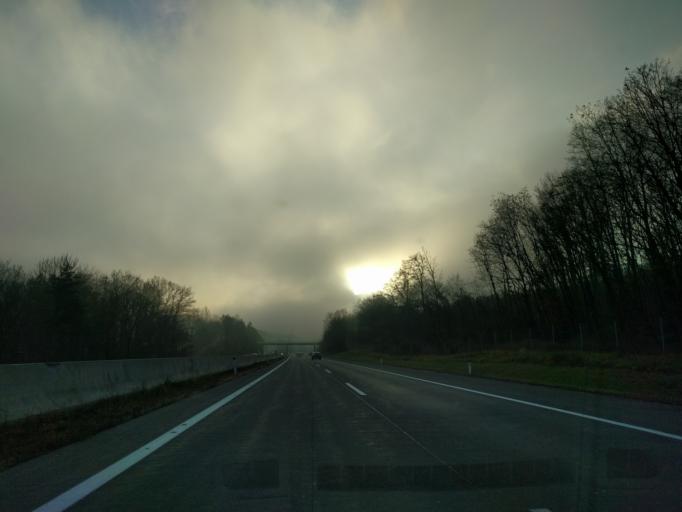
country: AT
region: Lower Austria
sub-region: Politischer Bezirk Wien-Umgebung
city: Purkersdorf
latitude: 48.1871
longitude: 16.1898
